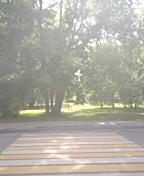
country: RU
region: Moscow
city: Pokrovskoye-Streshnevo
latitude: 55.8156
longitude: 37.4693
